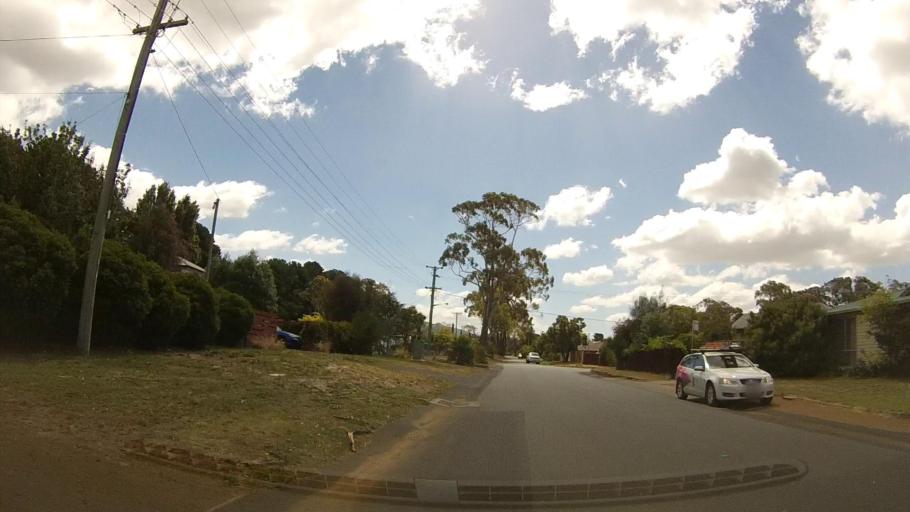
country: AU
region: Tasmania
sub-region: Clarence
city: Seven Mile Beach
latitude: -42.8592
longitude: 147.5015
